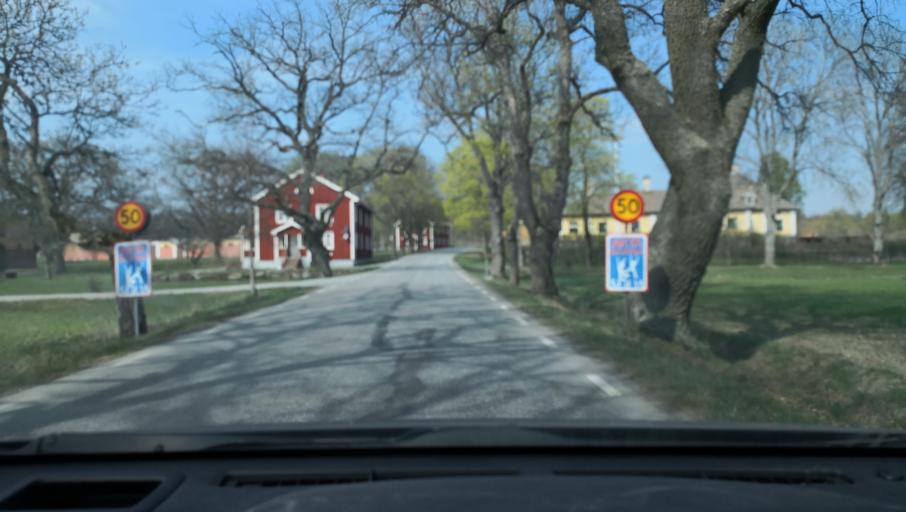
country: SE
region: Vaestmanland
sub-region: Vasteras
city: Skultuna
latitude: 59.7768
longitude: 16.3814
